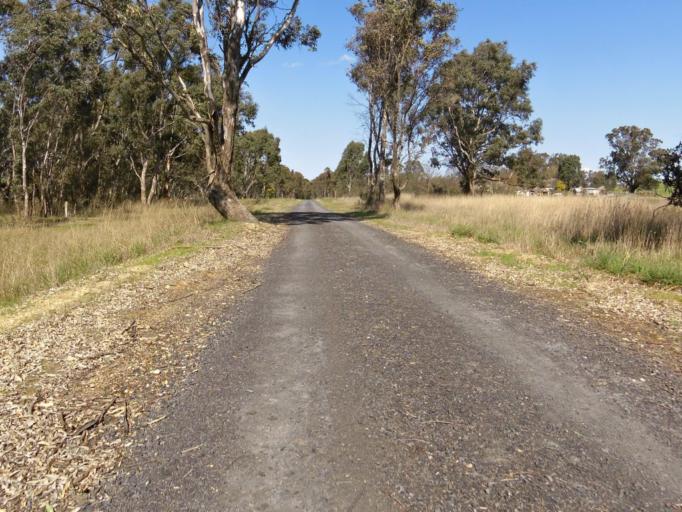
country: AU
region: Victoria
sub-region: Murrindindi
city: Alexandra
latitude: -36.9927
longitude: 145.7389
